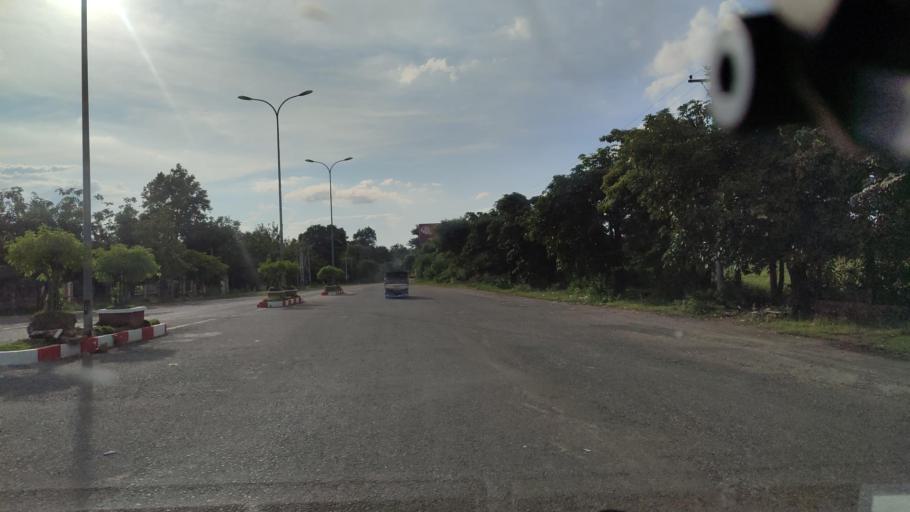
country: MM
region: Magway
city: Chauk
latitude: 20.8159
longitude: 95.1898
